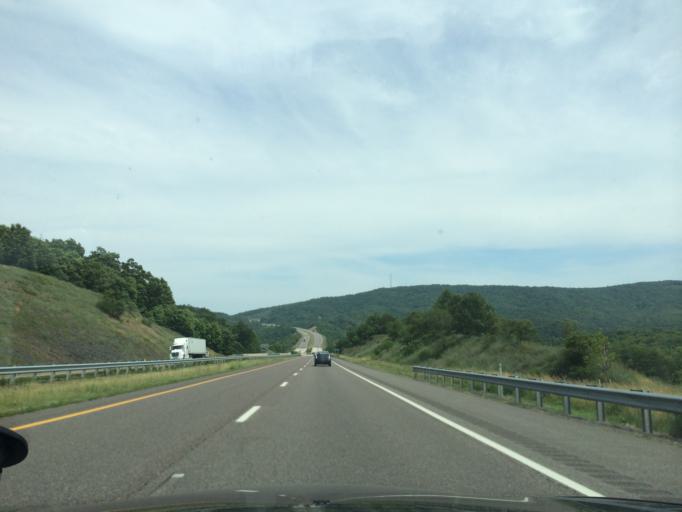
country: US
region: Maryland
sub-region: Allegany County
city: Cumberland
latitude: 39.6975
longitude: -78.5561
